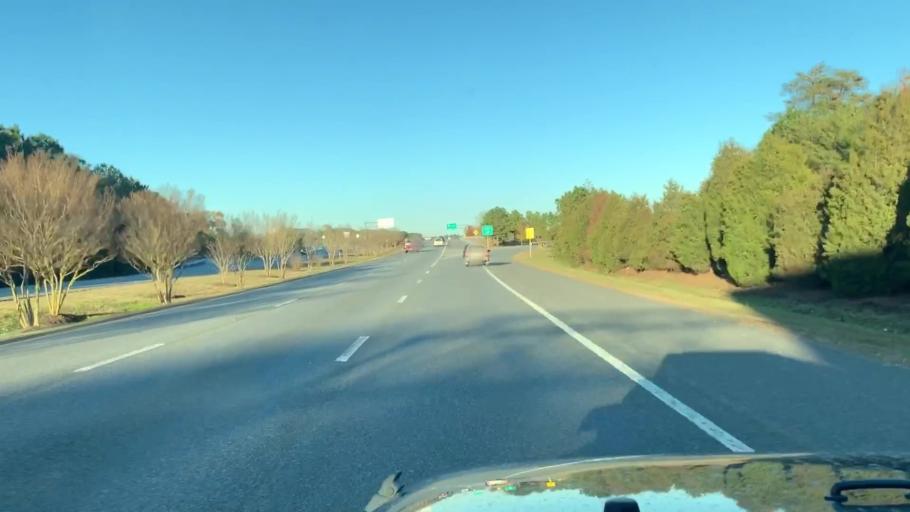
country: US
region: Virginia
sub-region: James City County
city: Williamsburg
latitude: 37.3413
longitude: -76.7455
